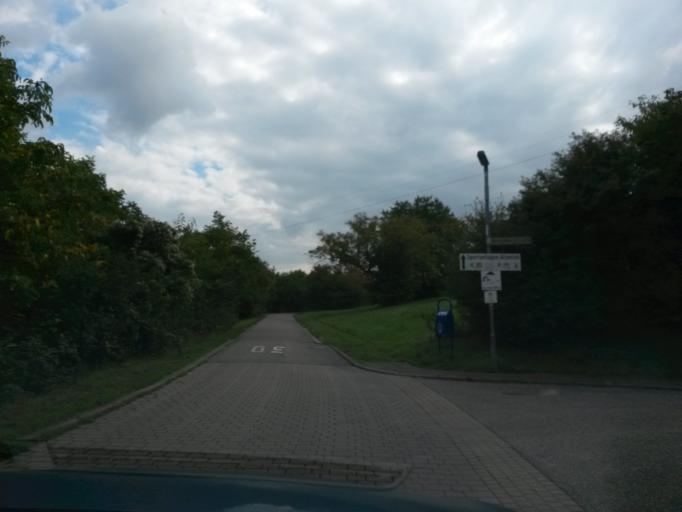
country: DE
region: Baden-Wuerttemberg
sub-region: Karlsruhe Region
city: Birkenfeld
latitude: 48.8923
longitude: 8.6006
